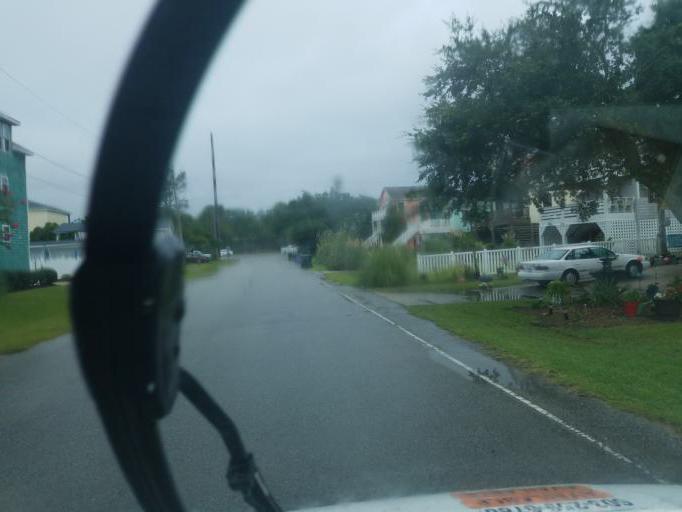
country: US
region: North Carolina
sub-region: Dare County
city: Nags Head
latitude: 35.9732
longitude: -75.6369
